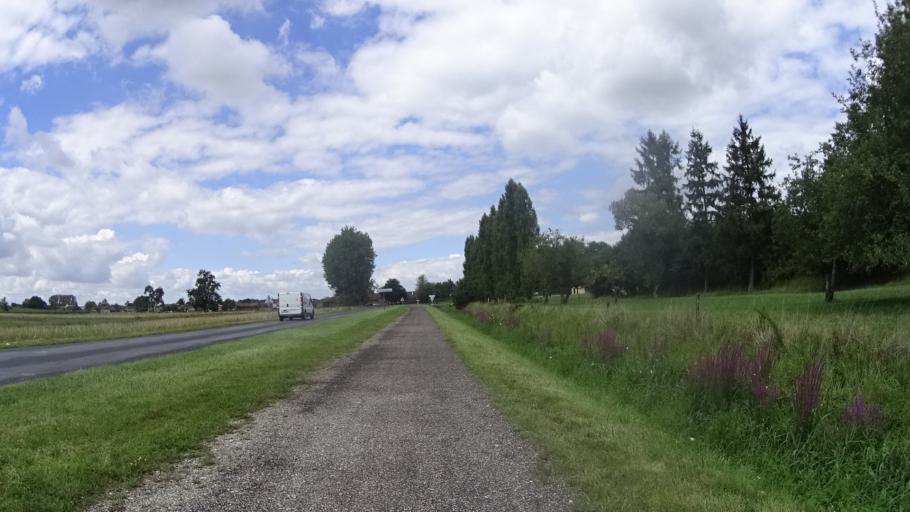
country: FR
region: Champagne-Ardenne
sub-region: Departement de la Haute-Marne
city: Montier-en-Der
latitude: 48.4762
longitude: 4.7619
